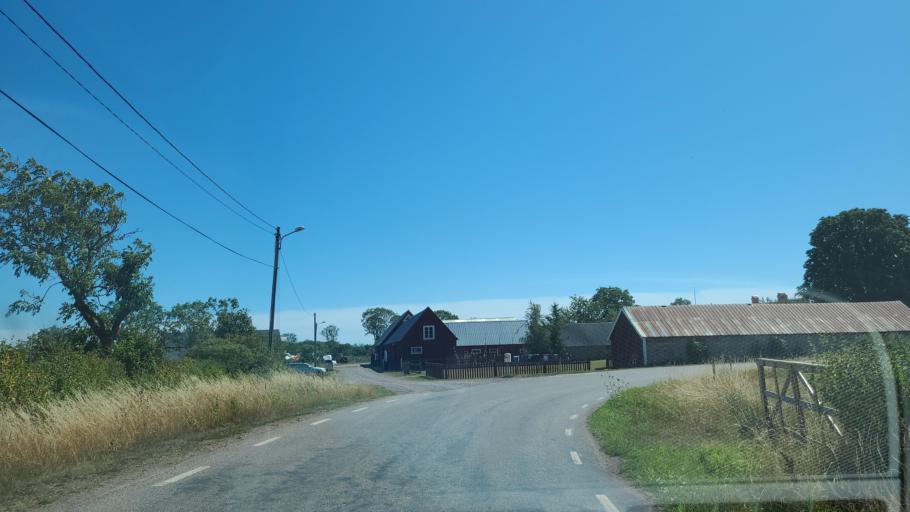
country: SE
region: Kalmar
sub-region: Borgholms Kommun
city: Borgholm
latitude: 56.7691
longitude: 16.6503
